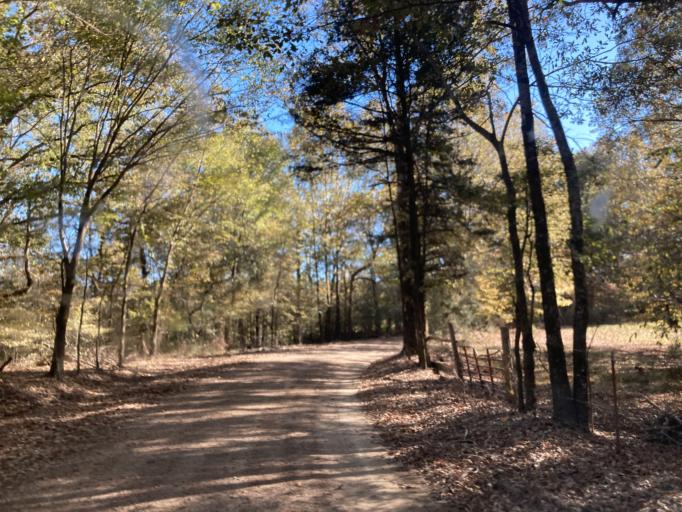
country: US
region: Mississippi
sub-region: Yazoo County
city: Yazoo City
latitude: 32.7570
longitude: -90.3883
